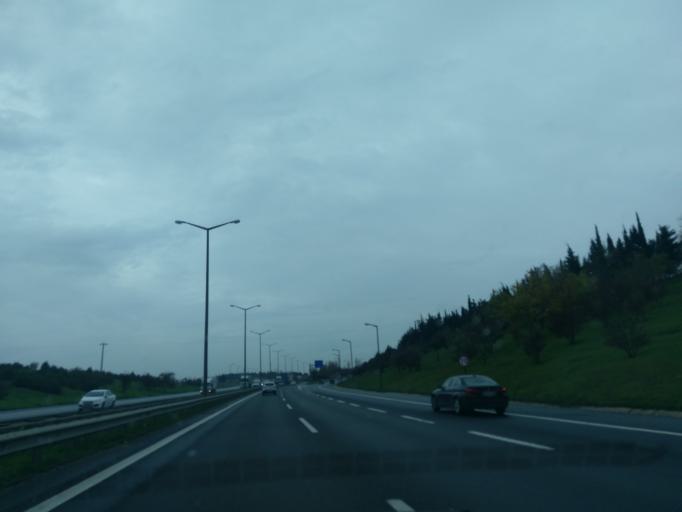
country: TR
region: Istanbul
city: Silivri
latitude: 41.1084
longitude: 28.2712
